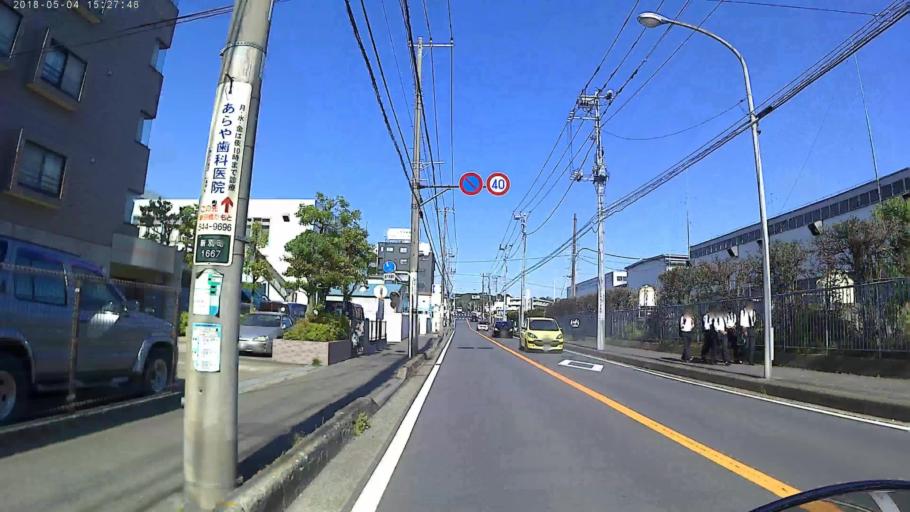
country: JP
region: Kanagawa
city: Yokohama
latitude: 35.5284
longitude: 139.6148
